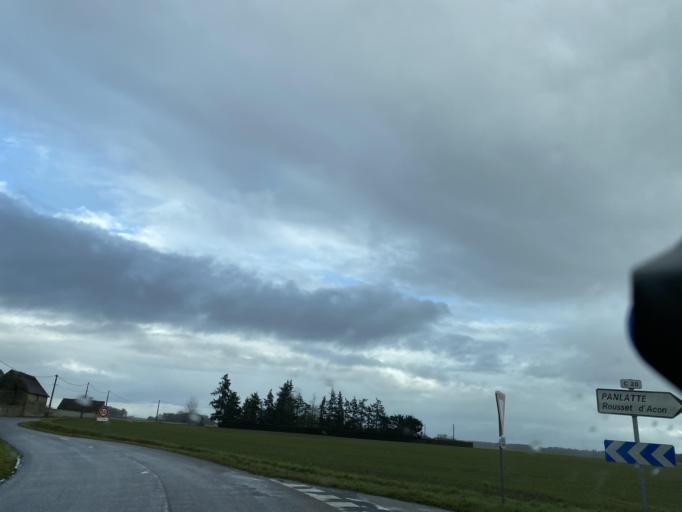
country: FR
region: Haute-Normandie
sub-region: Departement de l'Eure
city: Tillieres-sur-Avre
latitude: 48.7878
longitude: 1.0622
